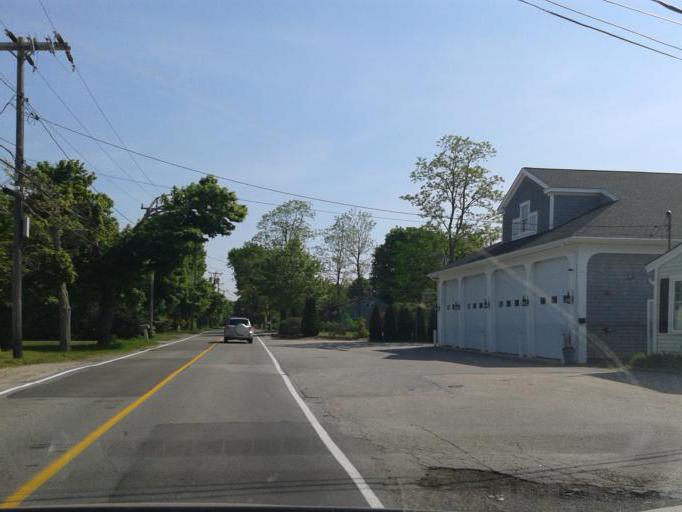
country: US
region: Massachusetts
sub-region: Barnstable County
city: East Falmouth
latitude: 41.5783
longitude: -70.5689
